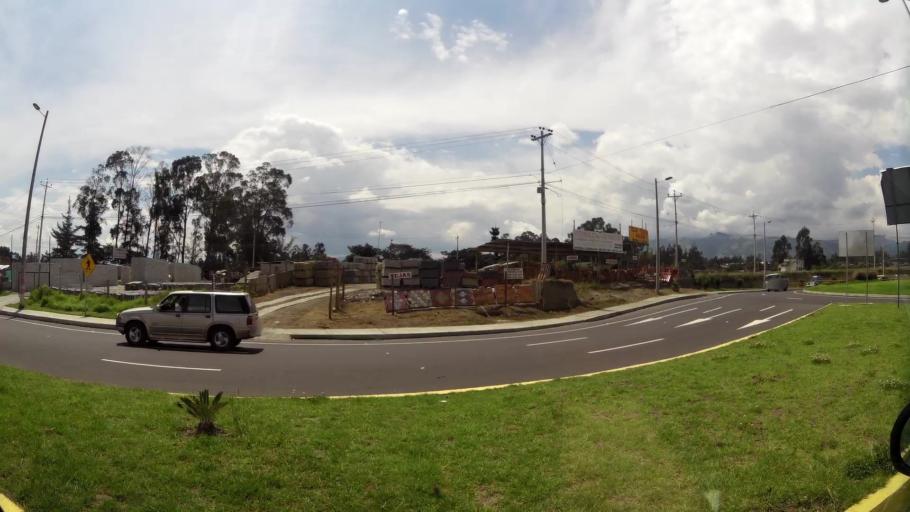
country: EC
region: Pichincha
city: Sangolqui
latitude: -0.2087
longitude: -78.3658
